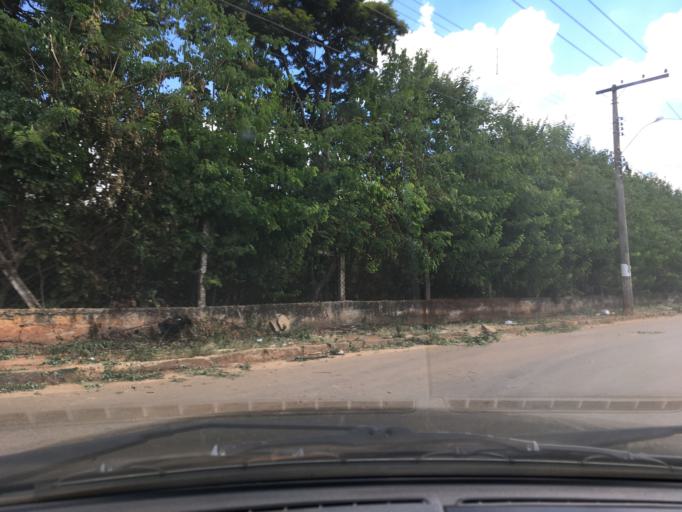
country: BR
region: Minas Gerais
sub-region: Mateus Leme
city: Mateus Leme
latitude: -19.9923
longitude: -44.4256
